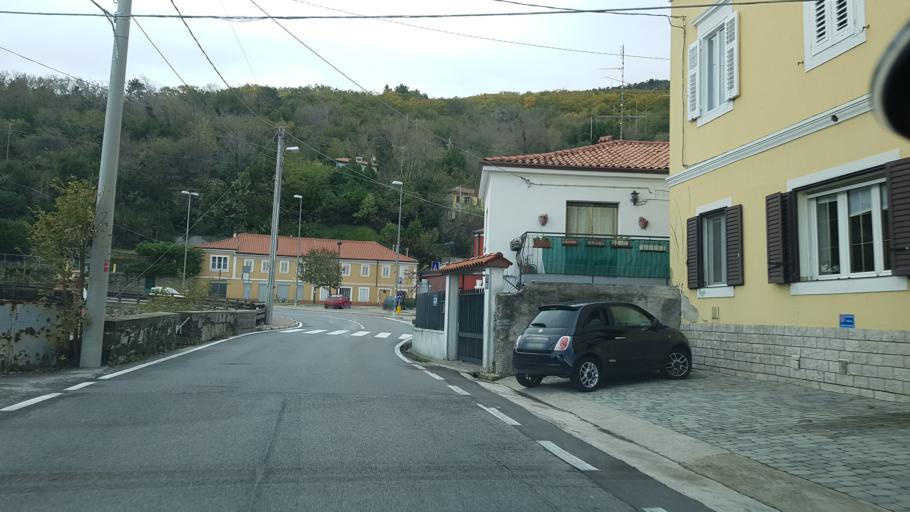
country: IT
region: Friuli Venezia Giulia
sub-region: Provincia di Trieste
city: Villa Opicina
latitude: 45.6789
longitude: 13.7618
